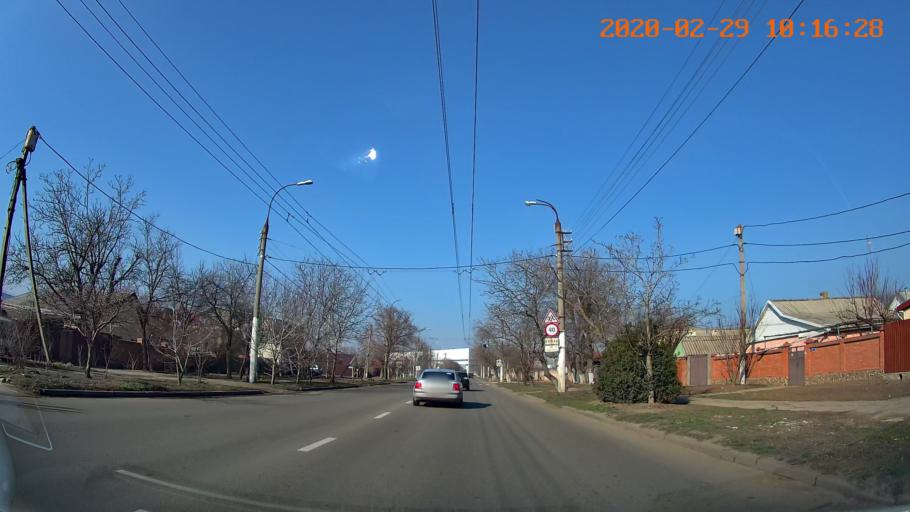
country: MD
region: Telenesti
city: Tiraspolul Nou
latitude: 46.8551
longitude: 29.6285
